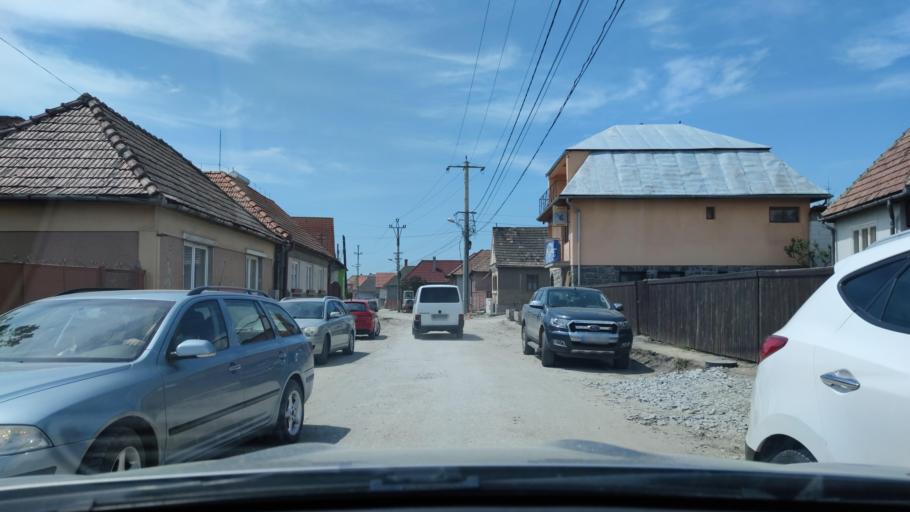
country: RO
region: Harghita
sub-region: Municipiul Gheorgheni
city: Gheorgheni
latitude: 46.7191
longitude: 25.5958
